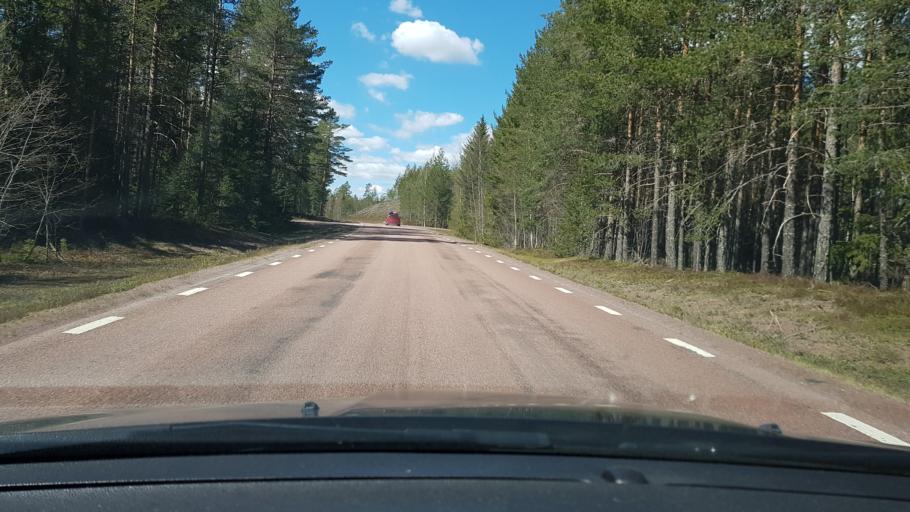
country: SE
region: Dalarna
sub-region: Alvdalens Kommun
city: AElvdalen
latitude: 61.1265
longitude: 14.0199
